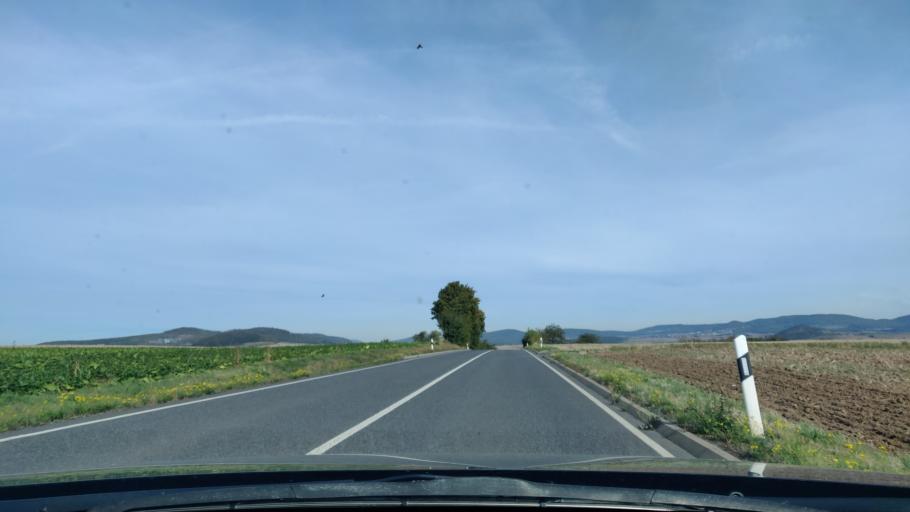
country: DE
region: Hesse
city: Fritzlar
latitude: 51.1468
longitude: 9.2731
